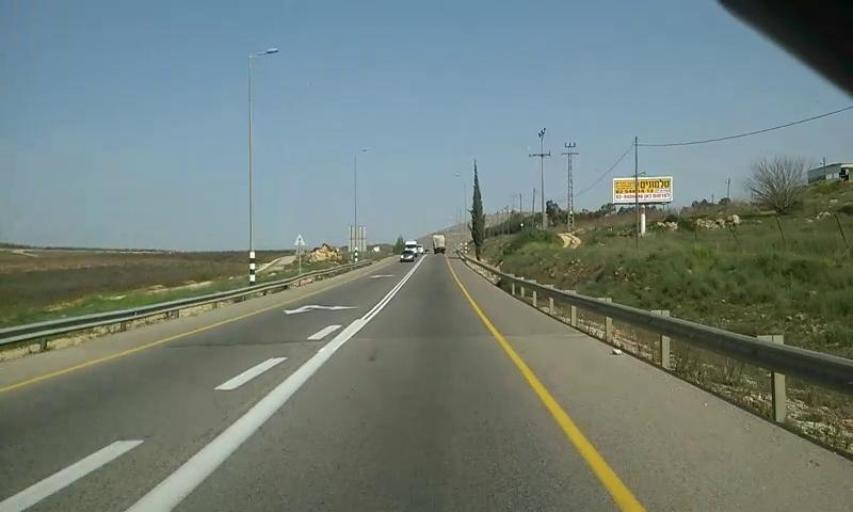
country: PS
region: West Bank
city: Qaryut
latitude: 32.0548
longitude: 35.2870
